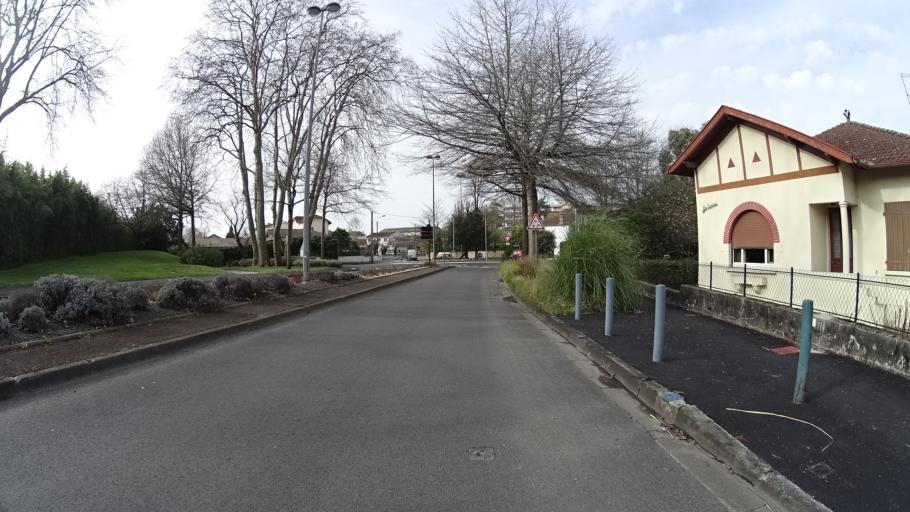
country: FR
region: Aquitaine
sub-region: Departement des Landes
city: Dax
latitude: 43.6992
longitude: -1.0545
